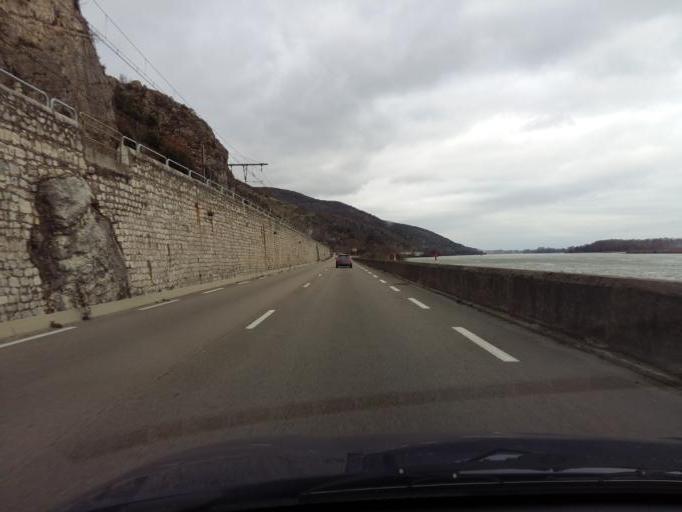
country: FR
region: Rhone-Alpes
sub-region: Departement de l'Ardeche
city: Le Pouzin
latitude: 44.7642
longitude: 4.7526
